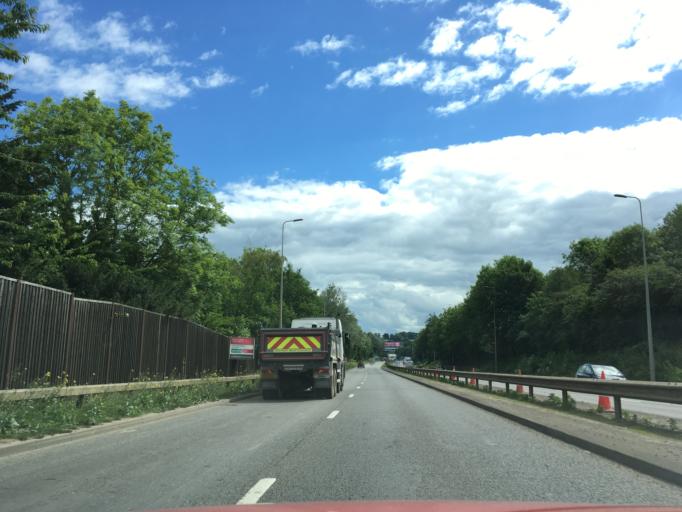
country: GB
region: England
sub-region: Oxfordshire
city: Banbury
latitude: 52.0716
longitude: -1.3273
